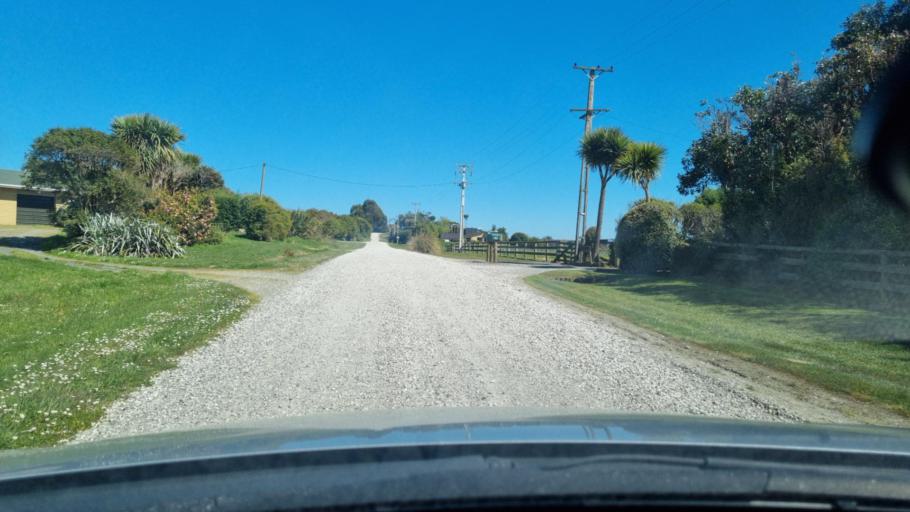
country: NZ
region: Southland
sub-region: Invercargill City
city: Invercargill
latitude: -46.4209
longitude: 168.2909
